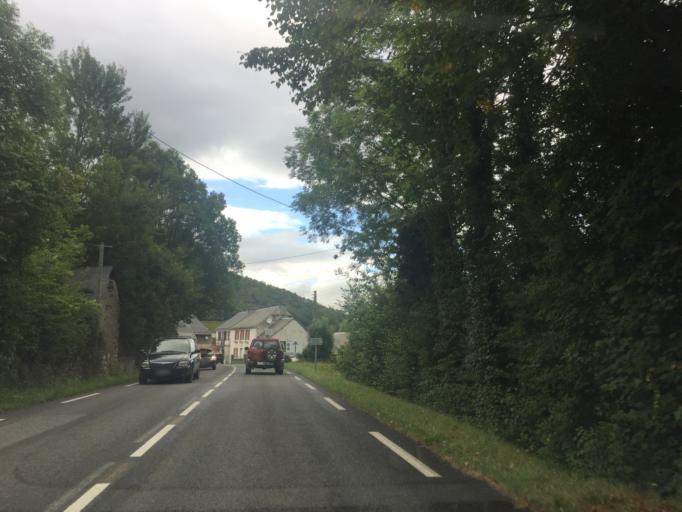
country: FR
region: Midi-Pyrenees
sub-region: Departement des Hautes-Pyrenees
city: La Barthe-de-Neste
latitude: 42.9928
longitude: 0.3748
